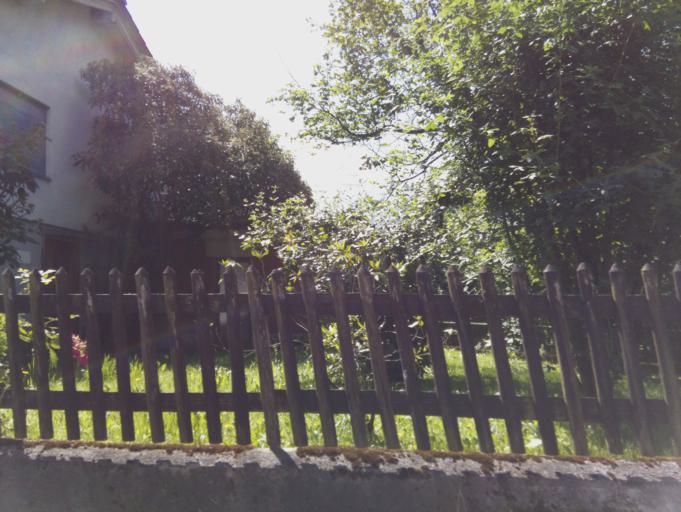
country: CH
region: Glarus
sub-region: Glarus
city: Oberurnen
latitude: 47.1166
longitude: 9.0613
